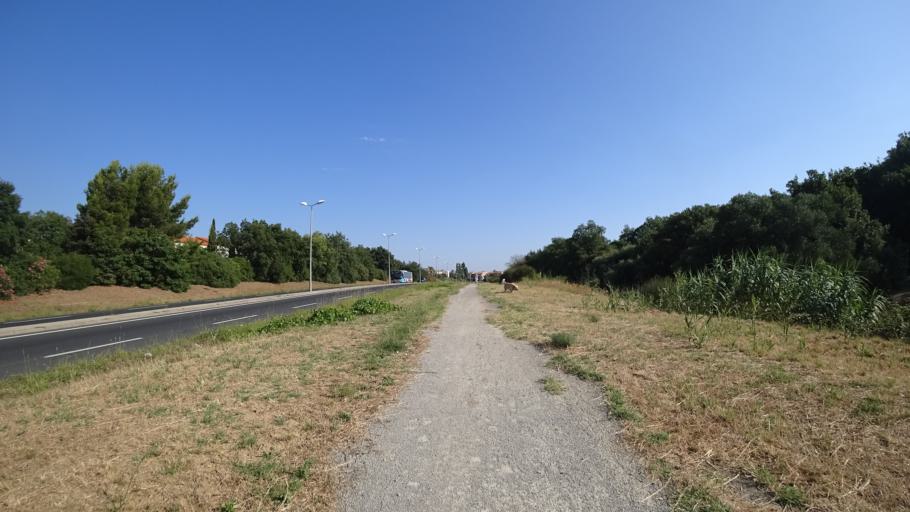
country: FR
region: Languedoc-Roussillon
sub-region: Departement des Pyrenees-Orientales
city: Cabestany
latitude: 42.6949
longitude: 2.9362
